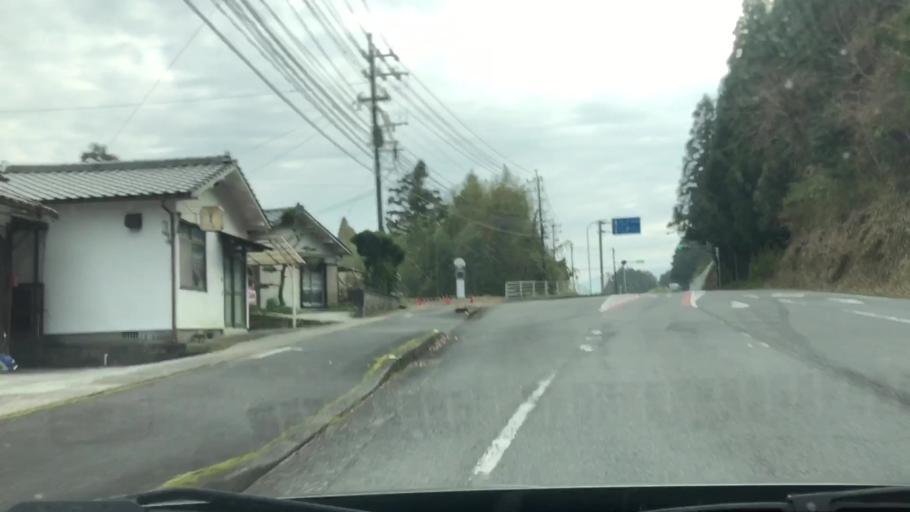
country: JP
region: Oita
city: Takedamachi
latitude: 32.9790
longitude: 131.5557
